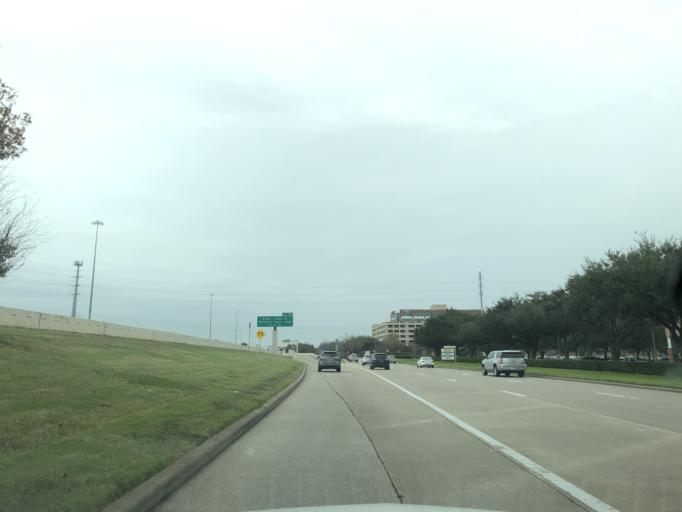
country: US
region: Texas
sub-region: Fort Bend County
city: Sugar Land
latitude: 29.5936
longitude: -95.6273
